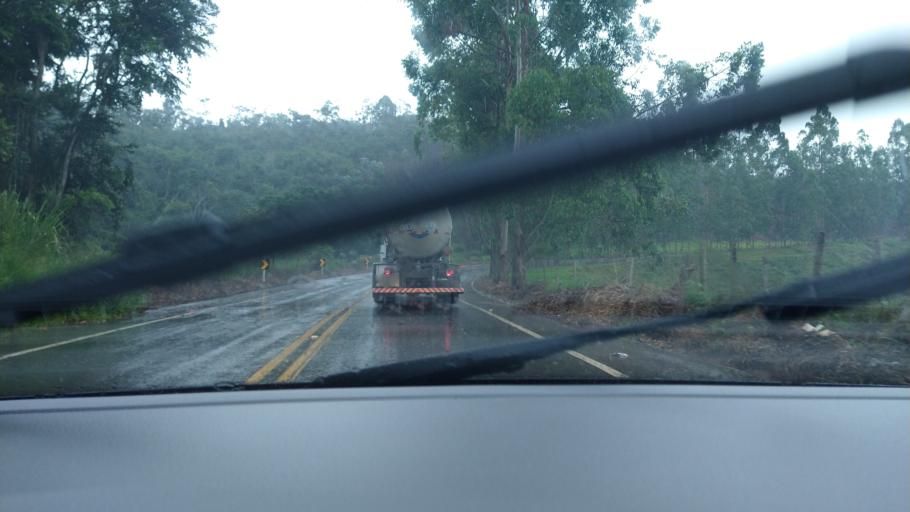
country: BR
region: Minas Gerais
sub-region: Ponte Nova
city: Ponte Nova
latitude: -20.5809
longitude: -42.8800
